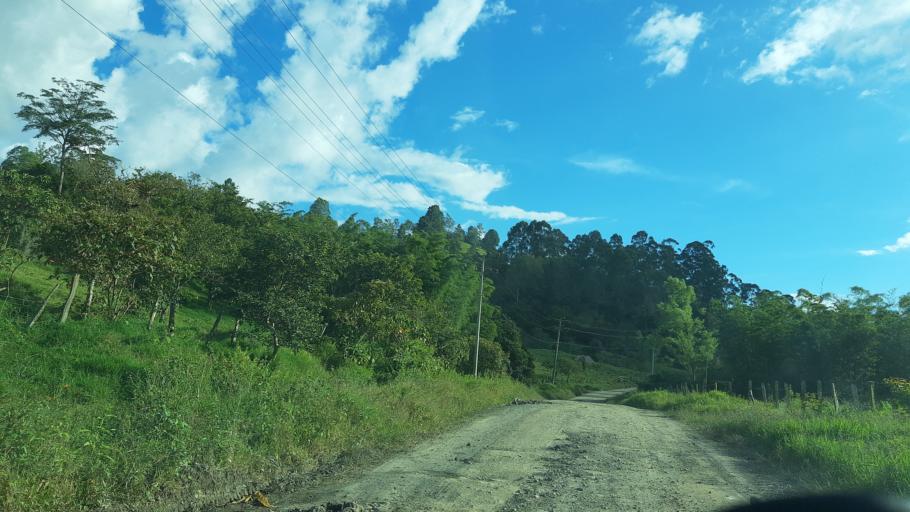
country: CO
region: Boyaca
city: Garagoa
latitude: 5.0812
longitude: -73.3712
